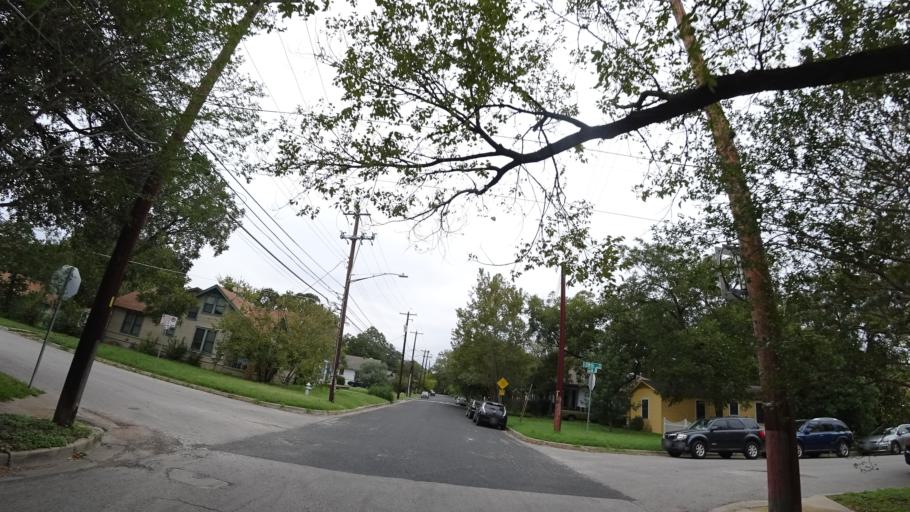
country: US
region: Texas
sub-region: Travis County
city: Austin
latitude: 30.2850
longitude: -97.7214
